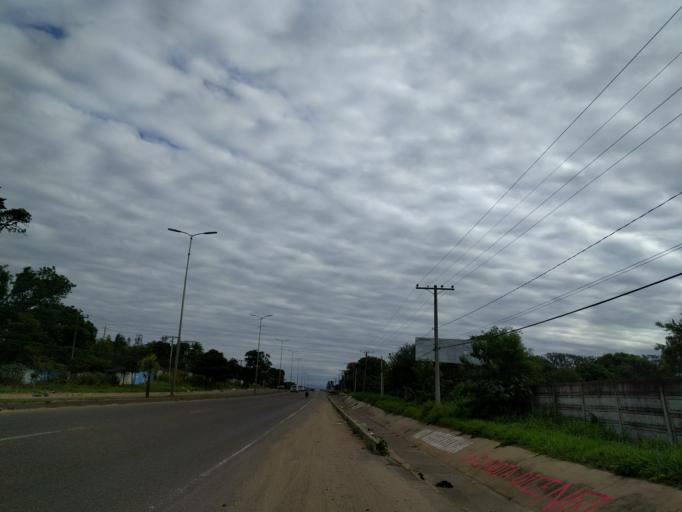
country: BO
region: Santa Cruz
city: Santa Cruz de la Sierra
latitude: -17.8553
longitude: -63.2576
